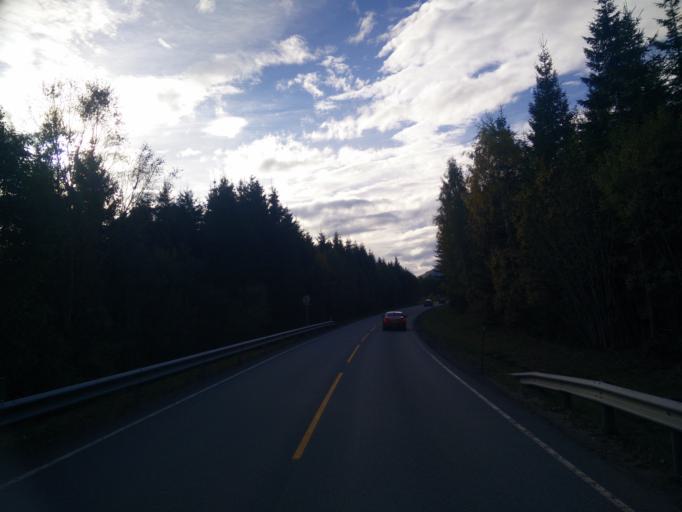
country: NO
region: More og Romsdal
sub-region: Vestnes
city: Vestnes
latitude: 62.6447
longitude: 7.0816
